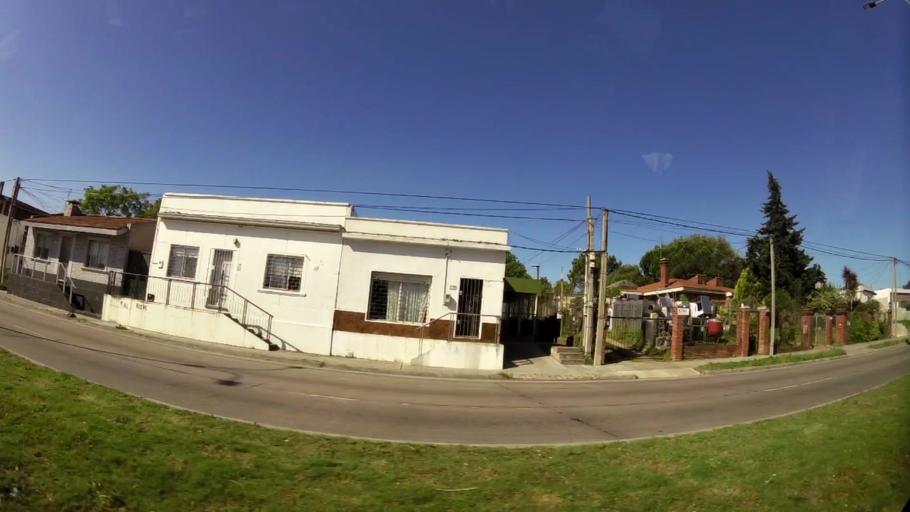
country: UY
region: Montevideo
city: Montevideo
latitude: -34.8364
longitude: -56.2051
